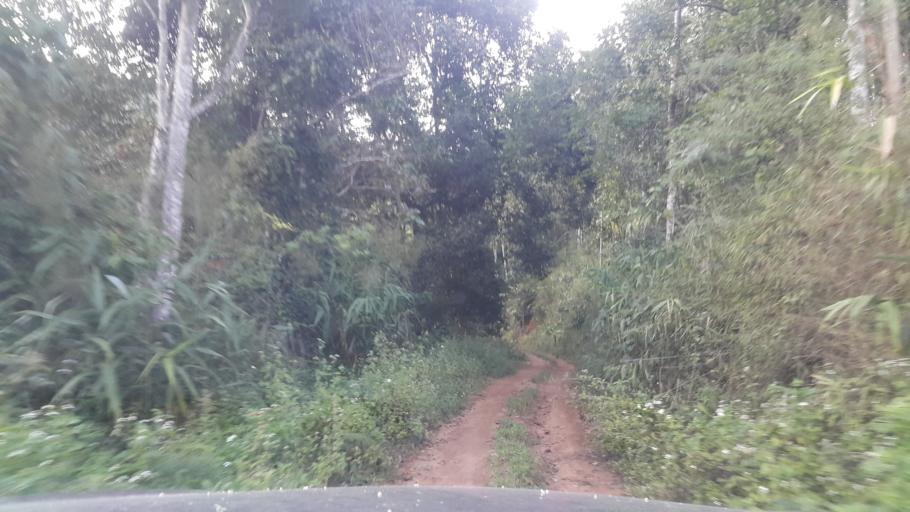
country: TH
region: Chiang Mai
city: Samoeng
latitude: 19.0189
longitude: 98.6517
